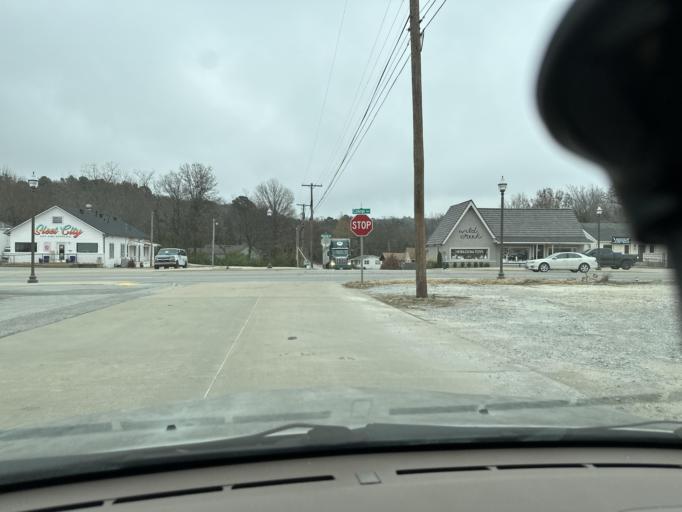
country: US
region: Arkansas
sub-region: Washington County
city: Fayetteville
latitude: 36.0753
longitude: -94.1575
